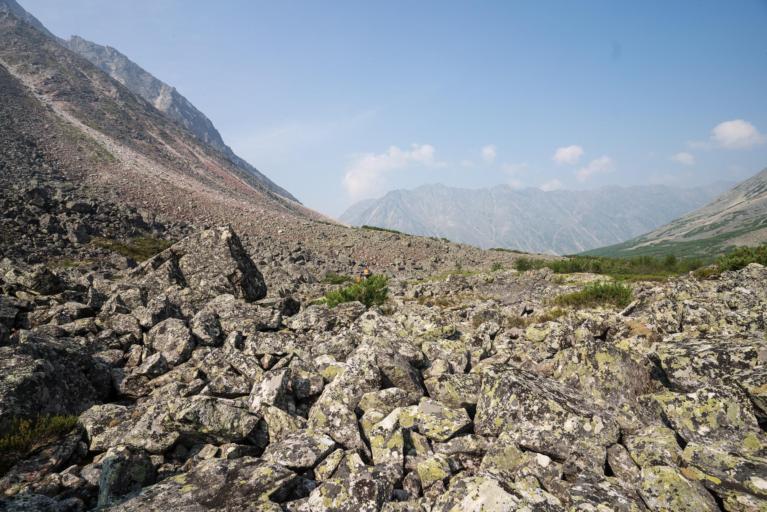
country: RU
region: Transbaikal Territory
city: Kuanda
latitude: 56.7870
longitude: 116.7870
